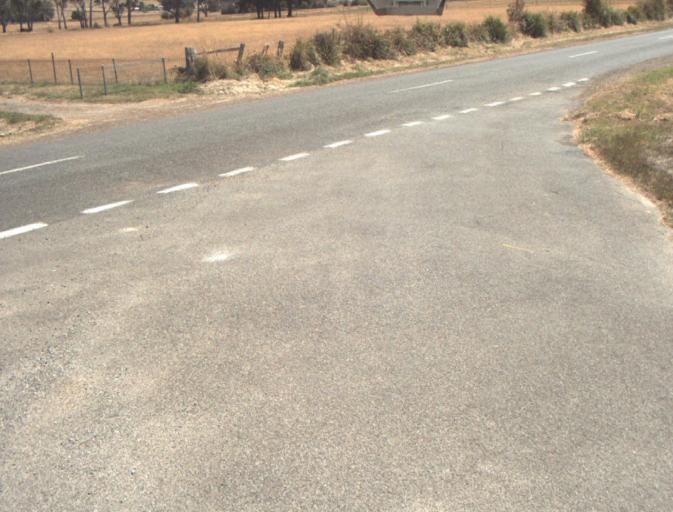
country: AU
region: Tasmania
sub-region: Launceston
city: Mayfield
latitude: -41.2528
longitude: 147.1474
